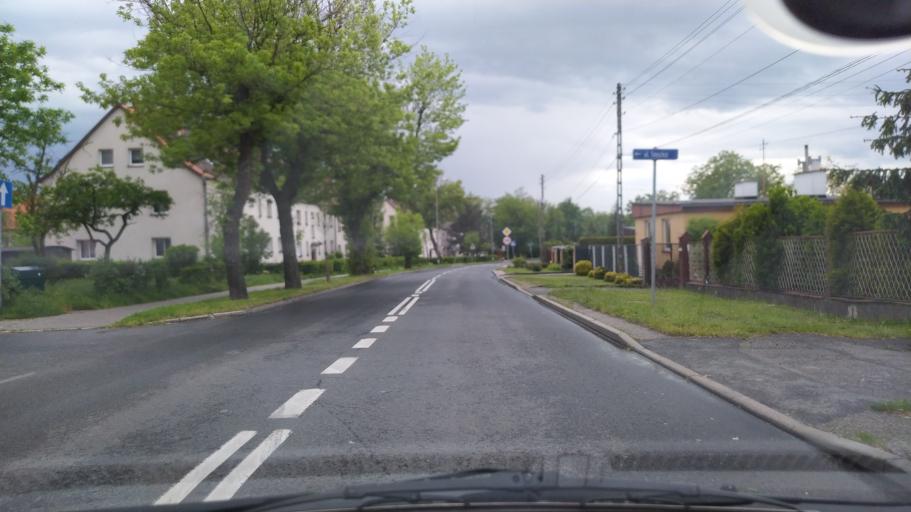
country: PL
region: Silesian Voivodeship
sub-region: Gliwice
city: Gliwice
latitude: 50.2917
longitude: 18.7212
